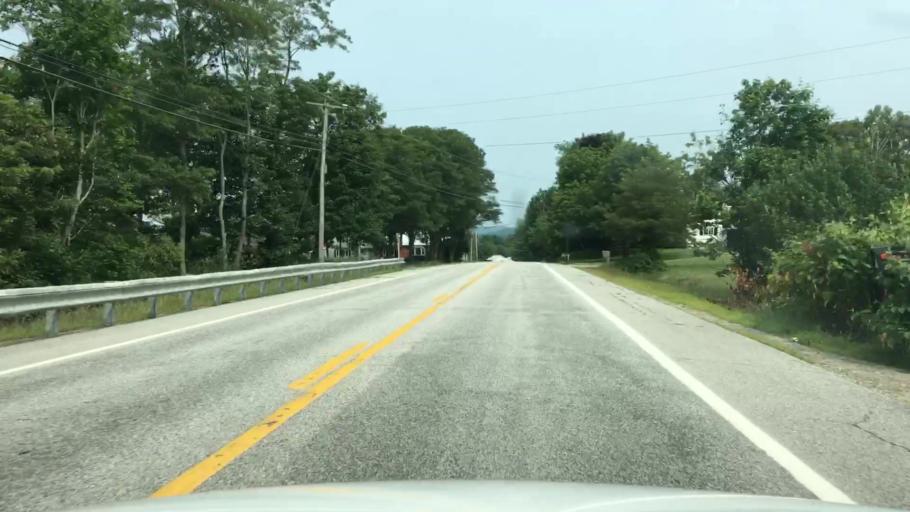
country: US
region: Maine
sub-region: Androscoggin County
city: Livermore Falls
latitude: 44.4375
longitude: -70.1478
